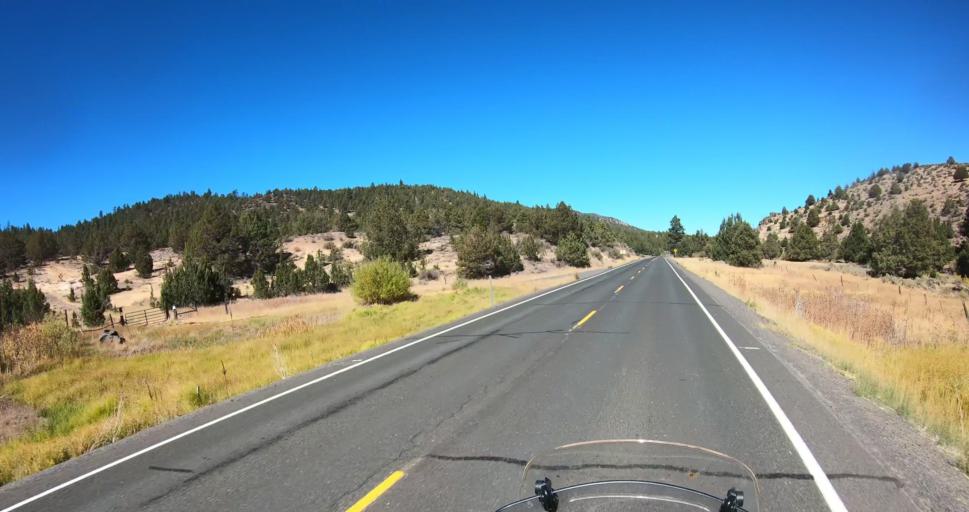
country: US
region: Oregon
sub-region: Lake County
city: Lakeview
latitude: 42.4184
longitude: -120.2899
